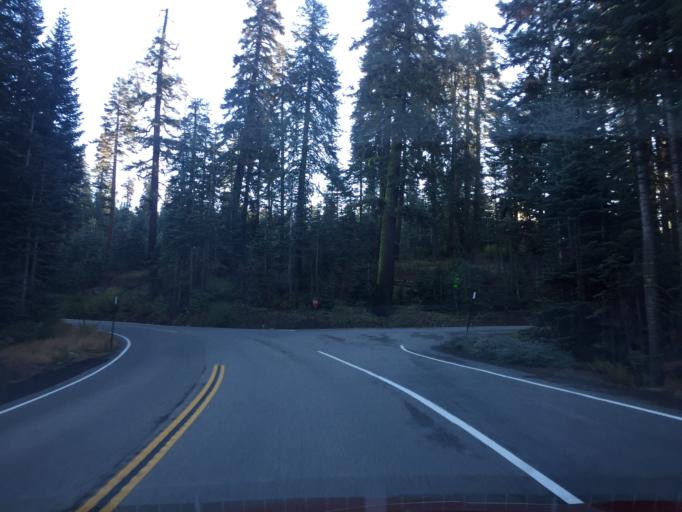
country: US
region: California
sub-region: Mariposa County
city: Yosemite Valley
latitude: 37.6641
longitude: -119.6654
